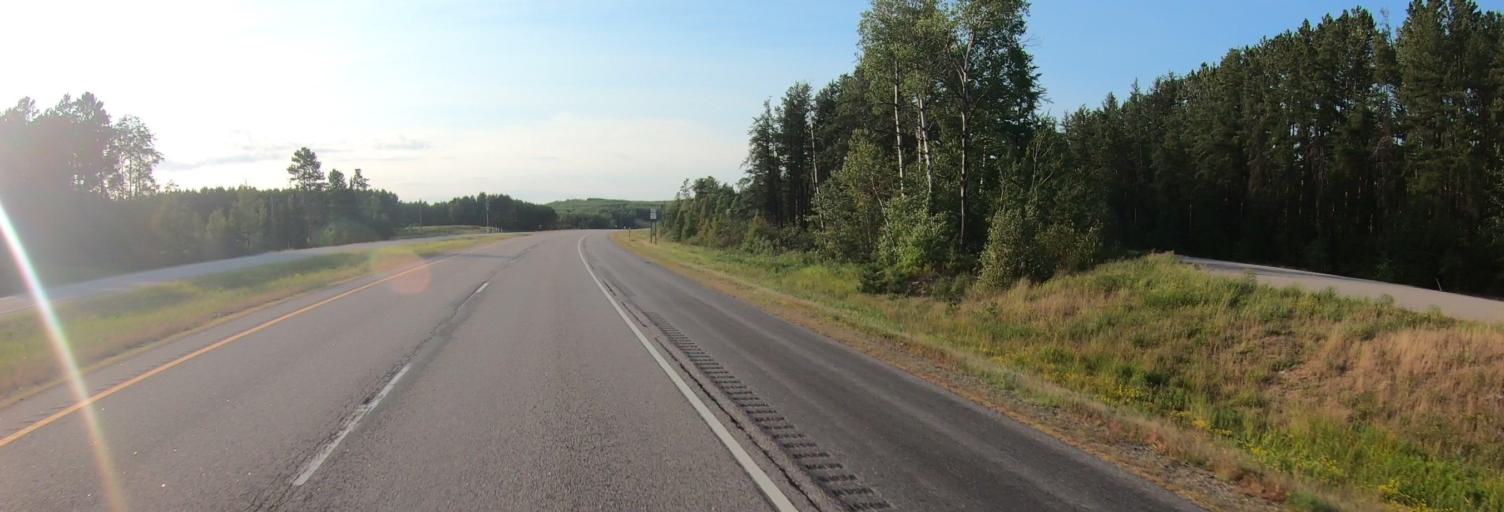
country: US
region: Minnesota
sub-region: Saint Louis County
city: Mountain Iron
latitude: 47.6738
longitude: -92.6329
